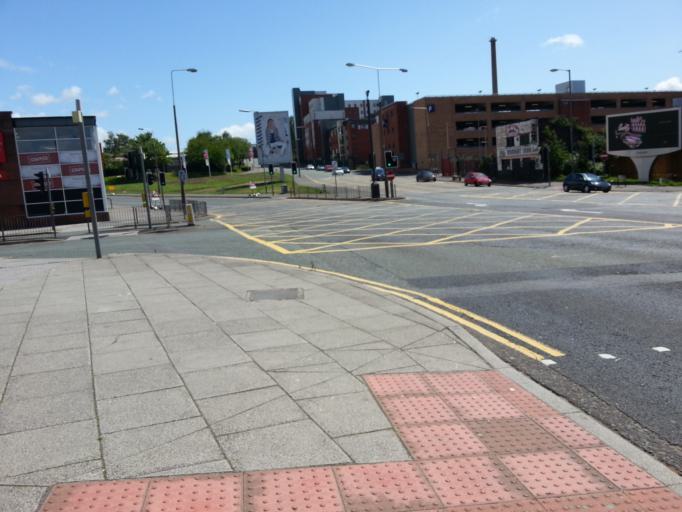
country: GB
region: England
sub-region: Liverpool
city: Liverpool
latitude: 53.4119
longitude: -2.9682
